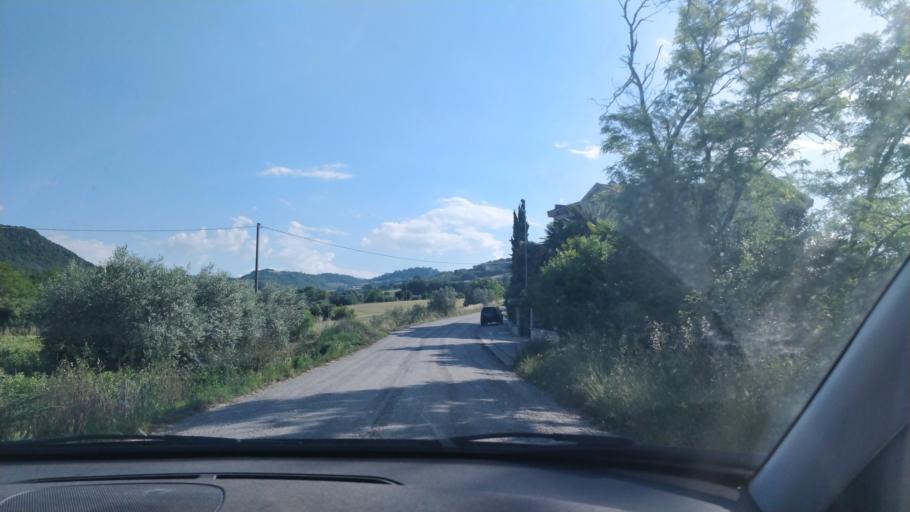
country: IT
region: The Marches
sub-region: Provincia di Ascoli Piceno
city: Massignano
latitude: 43.0334
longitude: 13.7980
